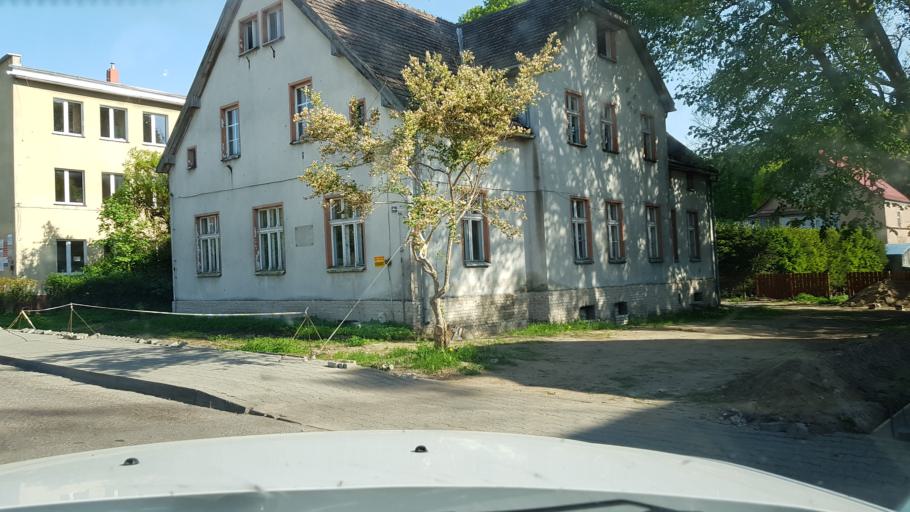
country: PL
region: West Pomeranian Voivodeship
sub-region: Powiat lobeski
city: Resko
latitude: 53.7721
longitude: 15.4084
